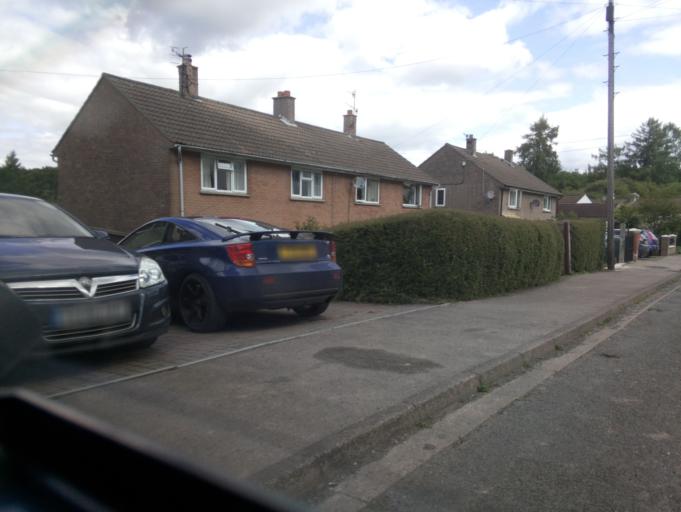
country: GB
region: England
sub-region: Gloucestershire
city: Bream
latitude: 51.7752
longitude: -2.5563
